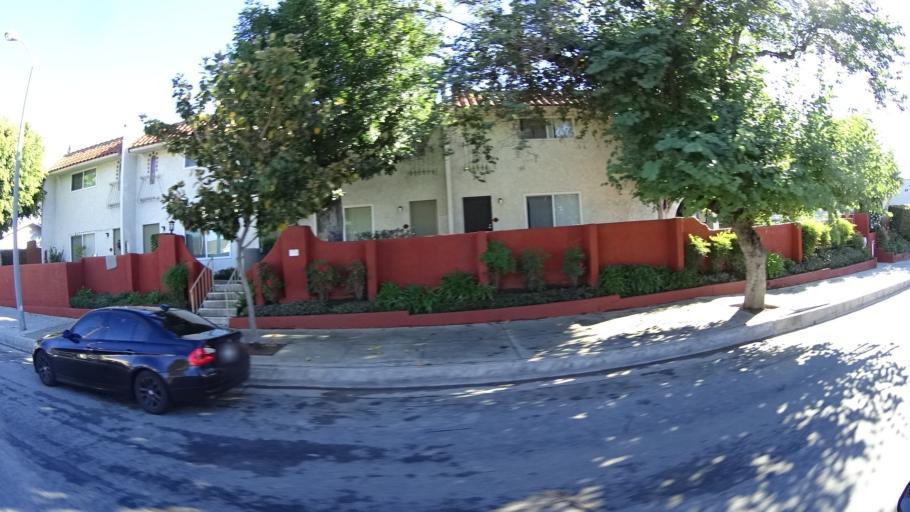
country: US
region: California
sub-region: Orange County
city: La Habra
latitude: 33.9408
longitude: -117.9418
